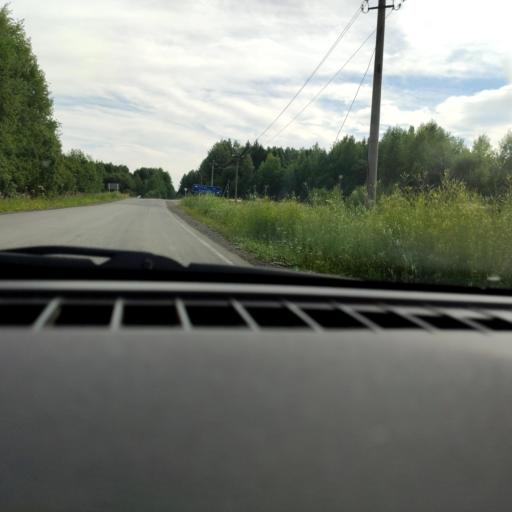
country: RU
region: Perm
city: Polazna
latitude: 58.3165
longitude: 56.1488
